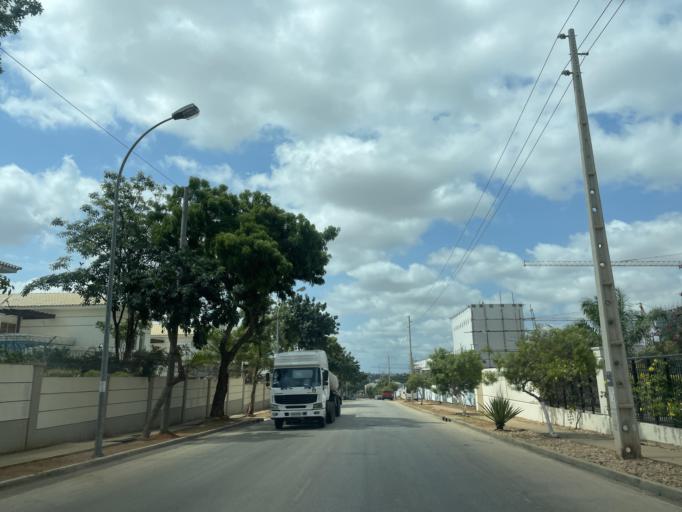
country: AO
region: Luanda
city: Luanda
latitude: -8.9284
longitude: 13.1840
